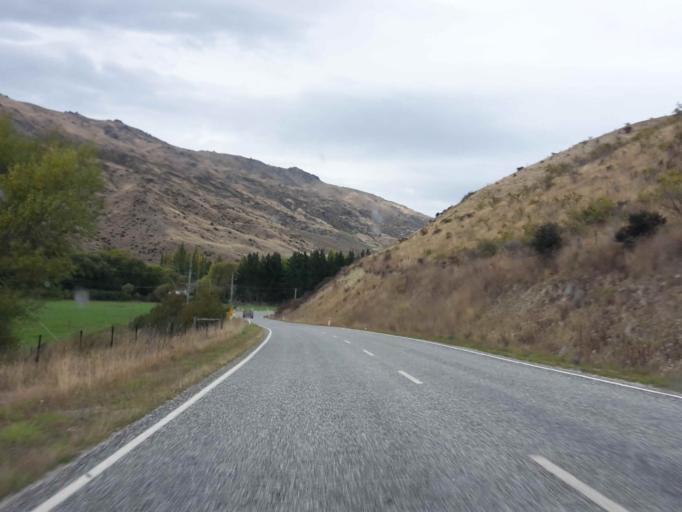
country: NZ
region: Otago
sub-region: Queenstown-Lakes District
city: Wanaka
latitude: -44.8277
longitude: 169.0606
